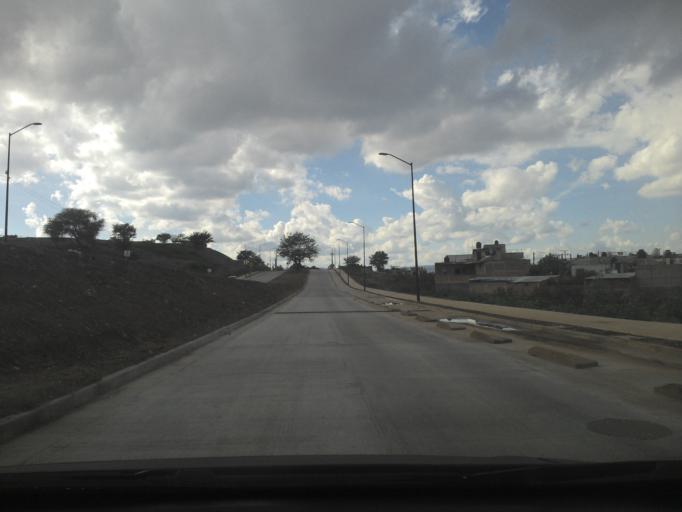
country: MX
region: Jalisco
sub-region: Tlajomulco de Zuniga
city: Altus Bosques
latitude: 20.6153
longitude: -103.3647
